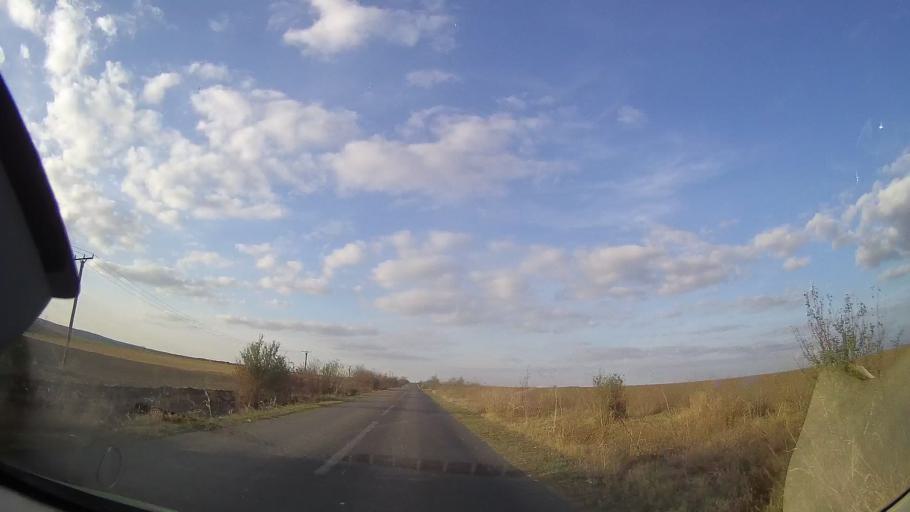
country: RO
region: Constanta
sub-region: Comuna Dumbraveni
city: Dumbraveni
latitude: 43.9296
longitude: 28.0286
